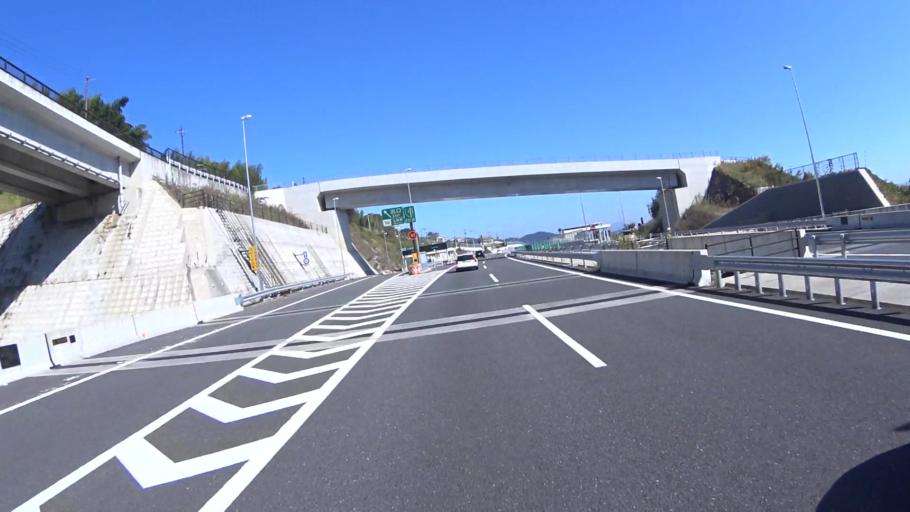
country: JP
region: Kyoto
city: Muko
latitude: 34.9647
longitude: 135.6552
